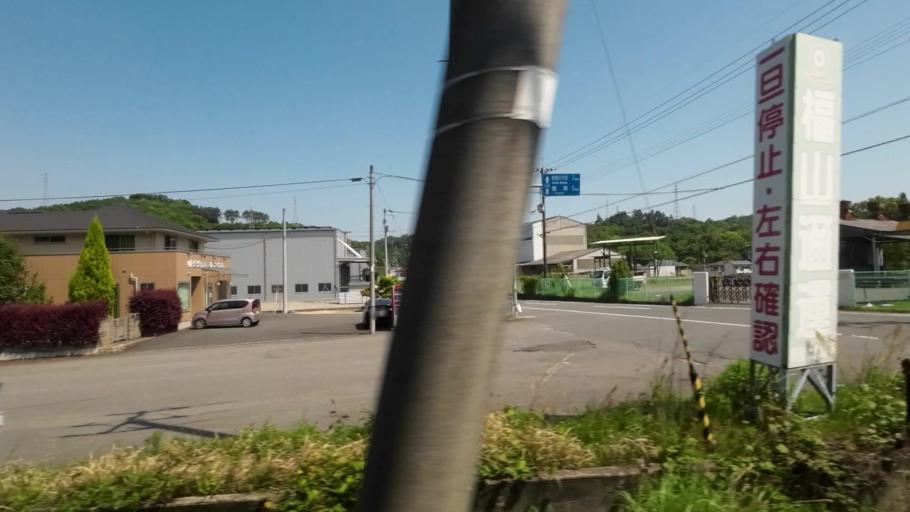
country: JP
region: Ehime
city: Niihama
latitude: 33.9279
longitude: 133.2618
